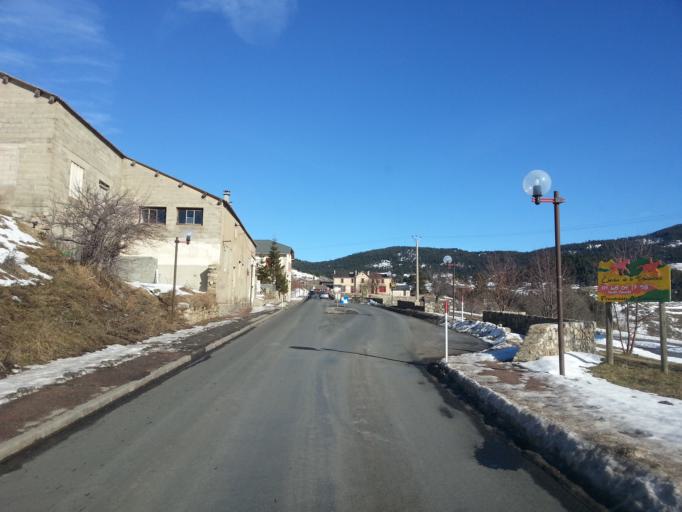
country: ES
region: Catalonia
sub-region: Provincia de Girona
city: Llivia
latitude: 42.5232
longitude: 2.1214
